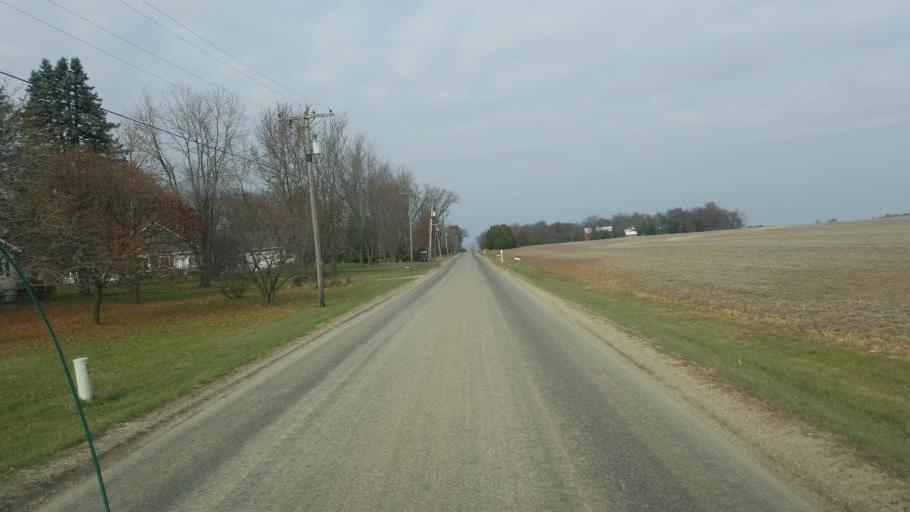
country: US
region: Indiana
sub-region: Adams County
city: Berne
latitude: 40.6449
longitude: -84.9357
